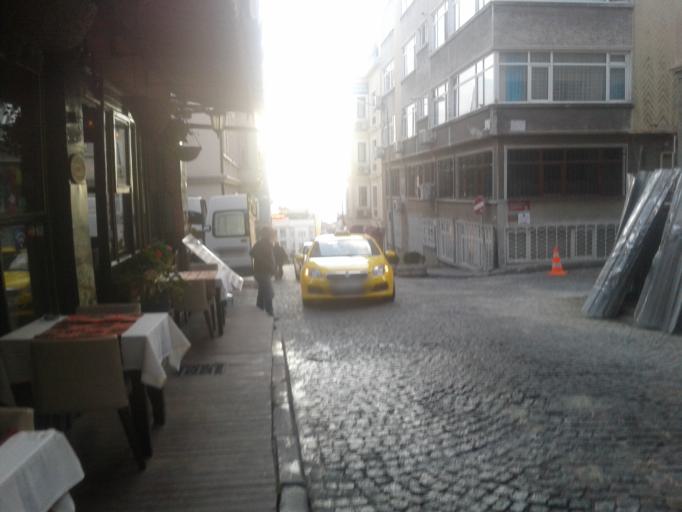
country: TR
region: Istanbul
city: Eminoenue
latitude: 41.0055
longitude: 28.9734
